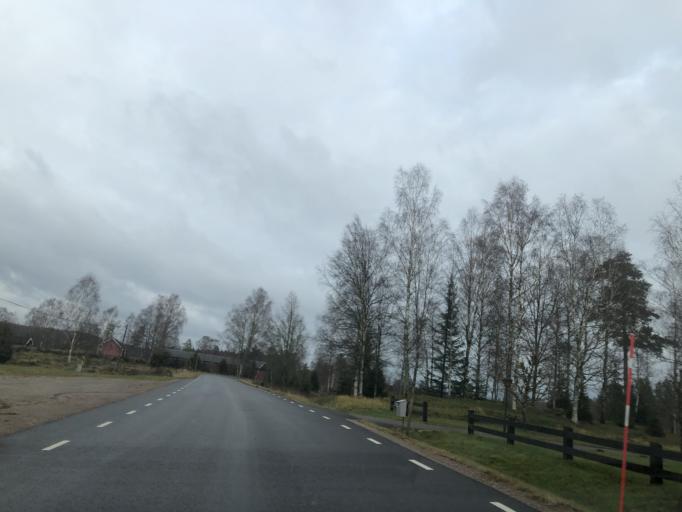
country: SE
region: Vaestra Goetaland
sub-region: Ulricehamns Kommun
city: Ulricehamn
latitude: 57.8333
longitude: 13.2623
